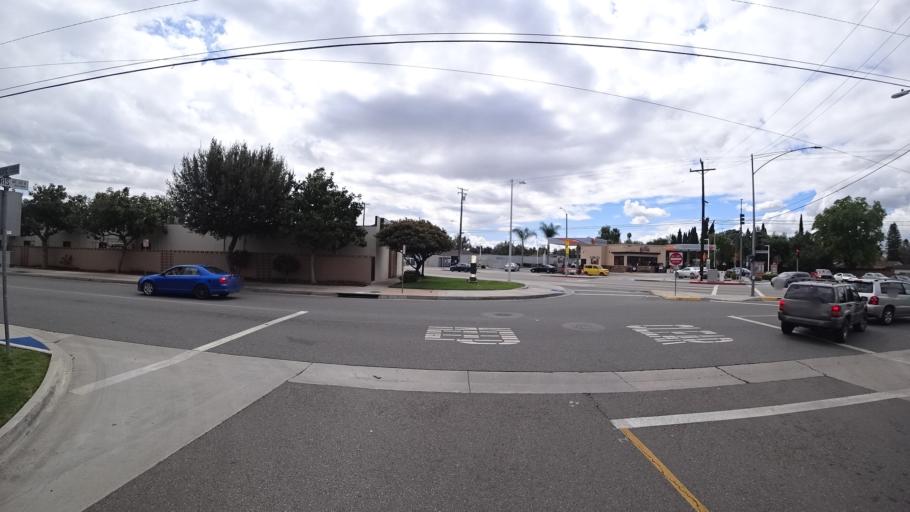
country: US
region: California
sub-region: Los Angeles County
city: West Covina
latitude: 34.0748
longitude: -117.9458
